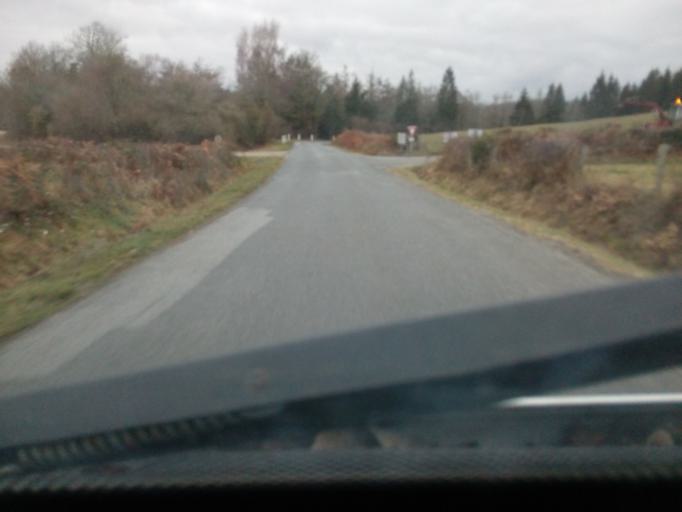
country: FR
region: Limousin
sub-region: Departement de la Creuse
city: Felletin
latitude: 45.8636
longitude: 2.2138
